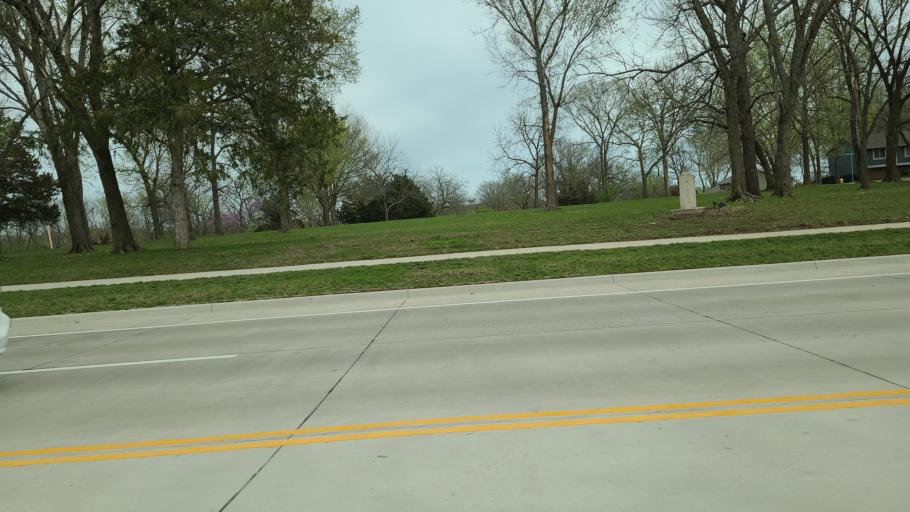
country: US
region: Kansas
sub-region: Douglas County
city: Lawrence
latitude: 38.9623
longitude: -95.2790
